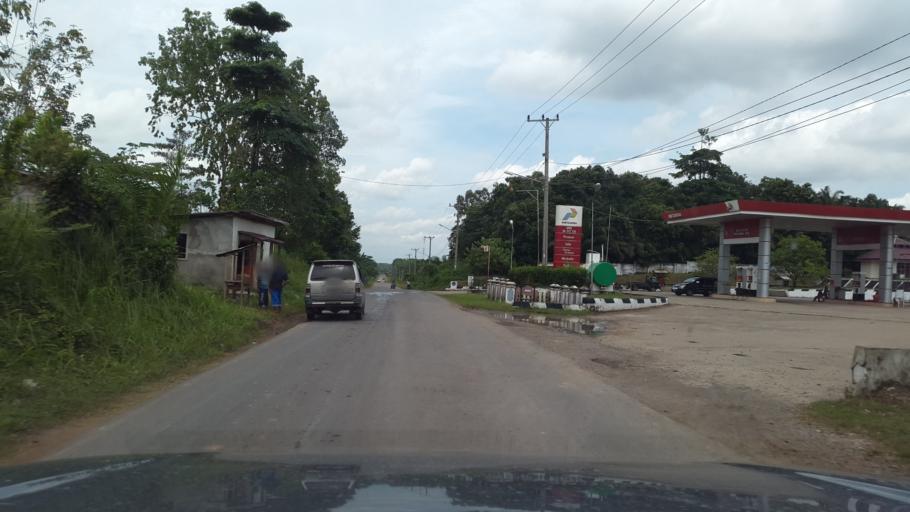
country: ID
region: South Sumatra
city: Gunungmegang Dalam
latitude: -3.3298
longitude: 103.9067
